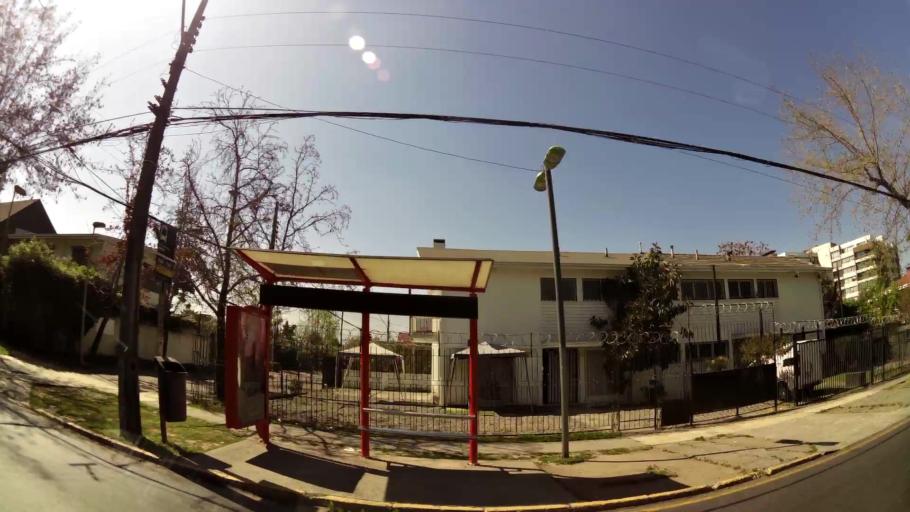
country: CL
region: Santiago Metropolitan
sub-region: Provincia de Santiago
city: Villa Presidente Frei, Nunoa, Santiago, Chile
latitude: -33.4295
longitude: -70.5646
